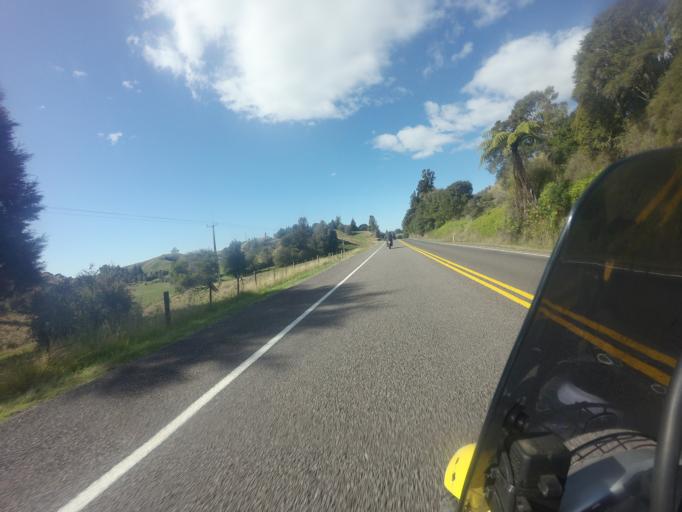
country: NZ
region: Bay of Plenty
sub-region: Opotiki District
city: Opotiki
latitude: -38.0531
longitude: 177.1385
